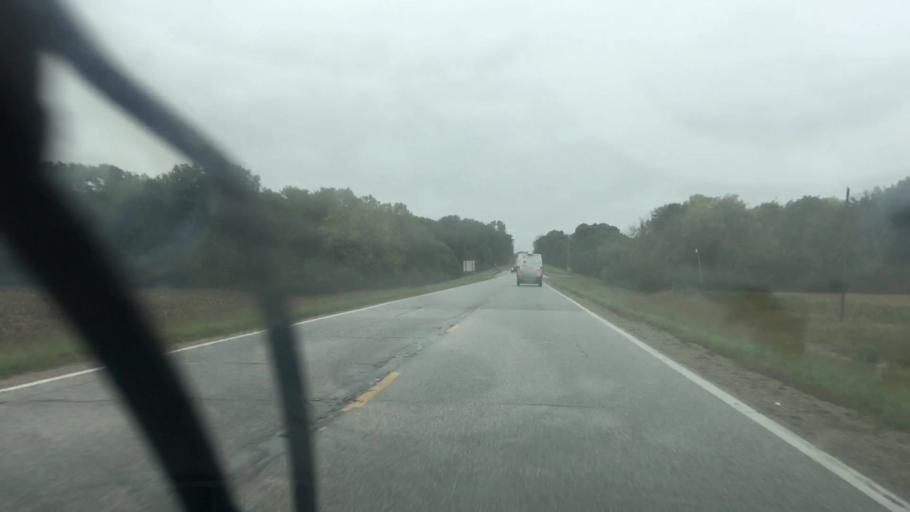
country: US
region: Kansas
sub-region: Anderson County
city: Garnett
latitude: 38.2519
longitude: -95.2486
